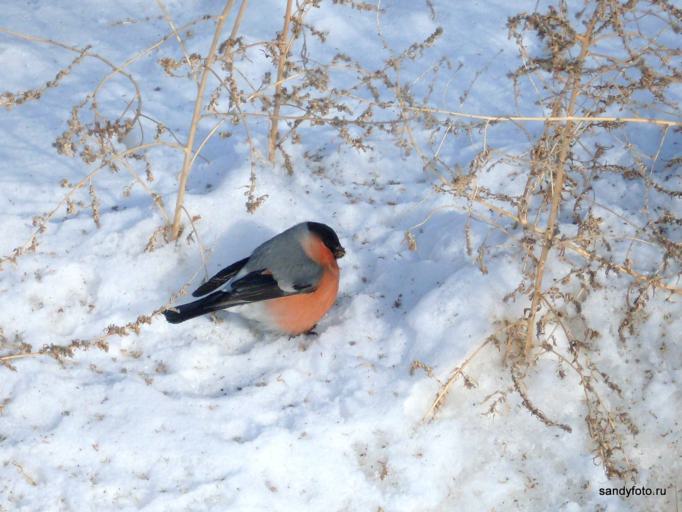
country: RU
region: Chelyabinsk
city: Troitsk
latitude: 54.1077
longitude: 61.5594
